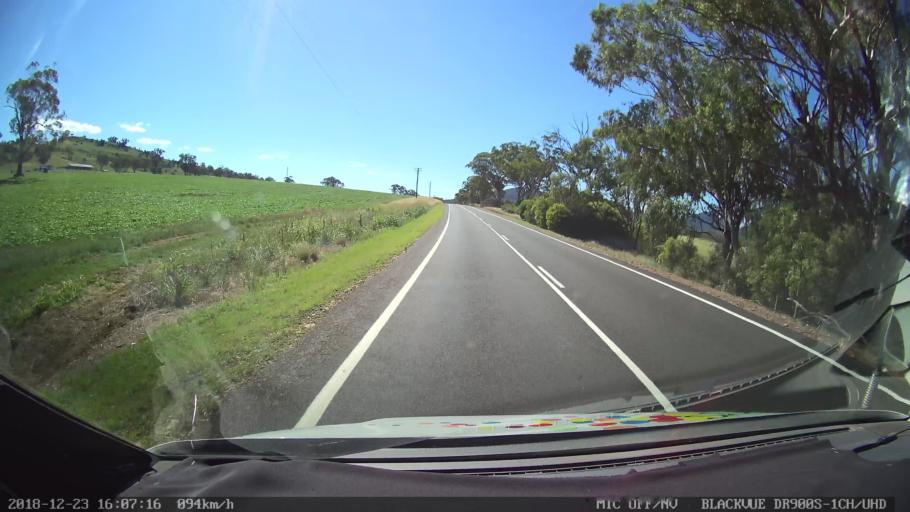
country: AU
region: New South Wales
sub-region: Tamworth Municipality
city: Phillip
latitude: -31.2726
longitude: 150.7645
